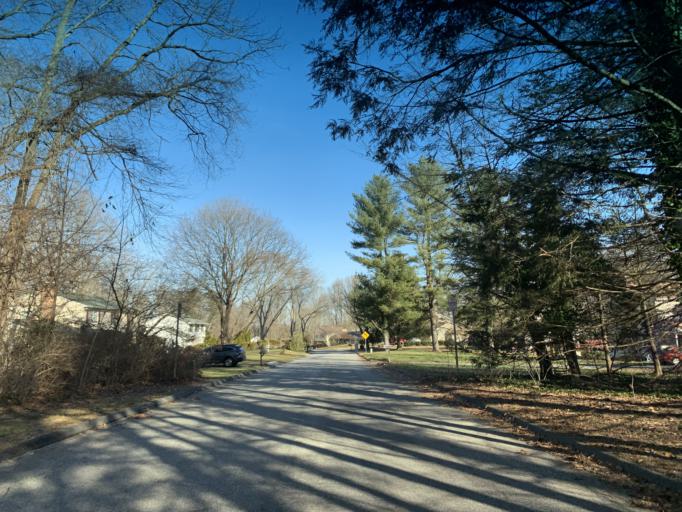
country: US
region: Maryland
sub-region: Harford County
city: South Bel Air
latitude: 39.5782
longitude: -76.2446
